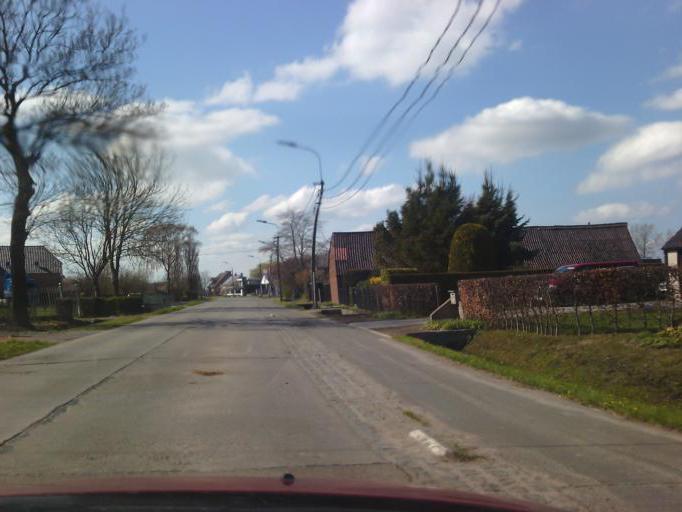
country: BE
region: Flanders
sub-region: Provincie Oost-Vlaanderen
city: Lokeren
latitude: 51.0835
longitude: 3.9506
